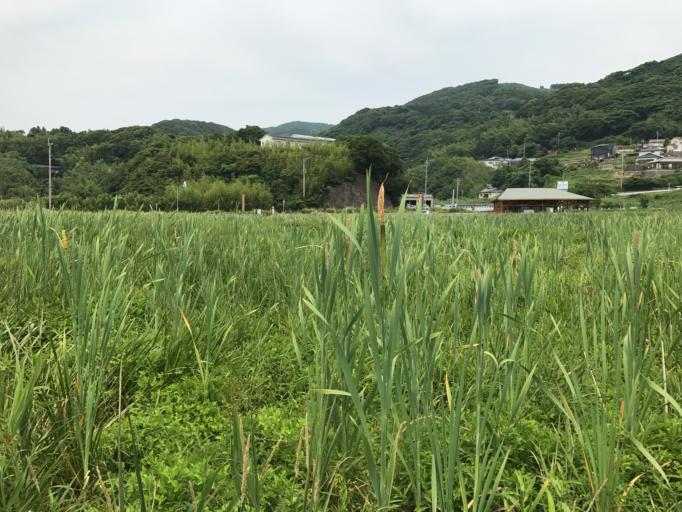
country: JP
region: Nagasaki
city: Togitsu
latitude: 32.8297
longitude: 129.7203
